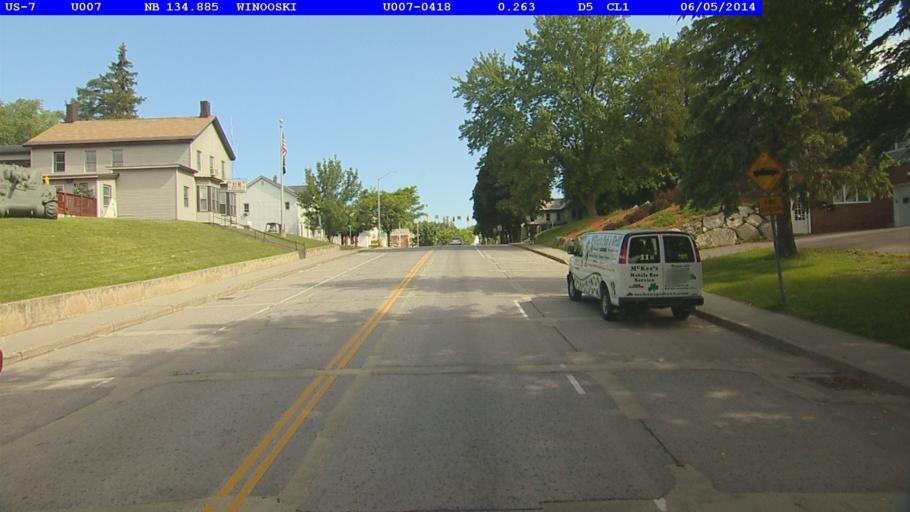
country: US
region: Vermont
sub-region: Chittenden County
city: Winooski
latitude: 44.4923
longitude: -73.1864
